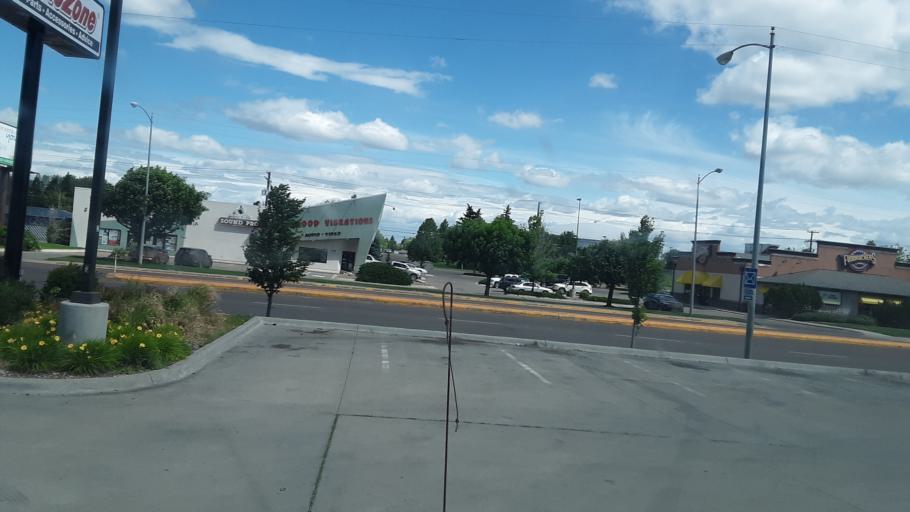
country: US
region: Montana
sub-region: Cascade County
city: Great Falls
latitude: 47.4935
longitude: -111.2498
